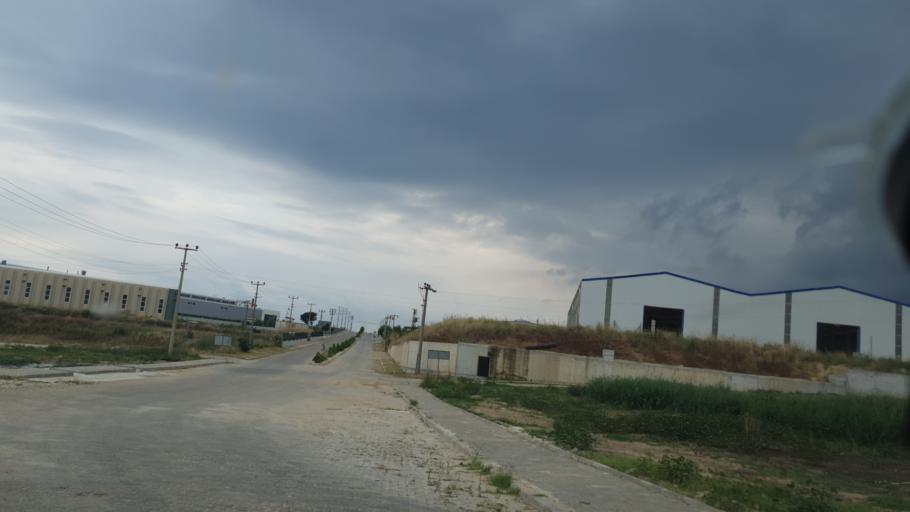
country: TR
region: Tekirdag
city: Hayrabolu
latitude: 41.2262
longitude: 27.0476
